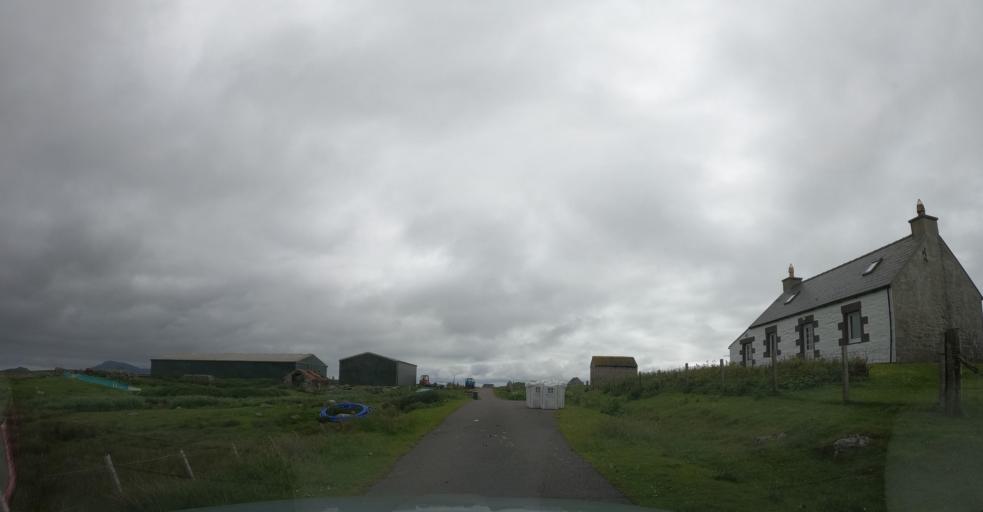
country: GB
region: Scotland
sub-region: Eilean Siar
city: Isle of North Uist
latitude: 57.5490
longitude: -7.3467
